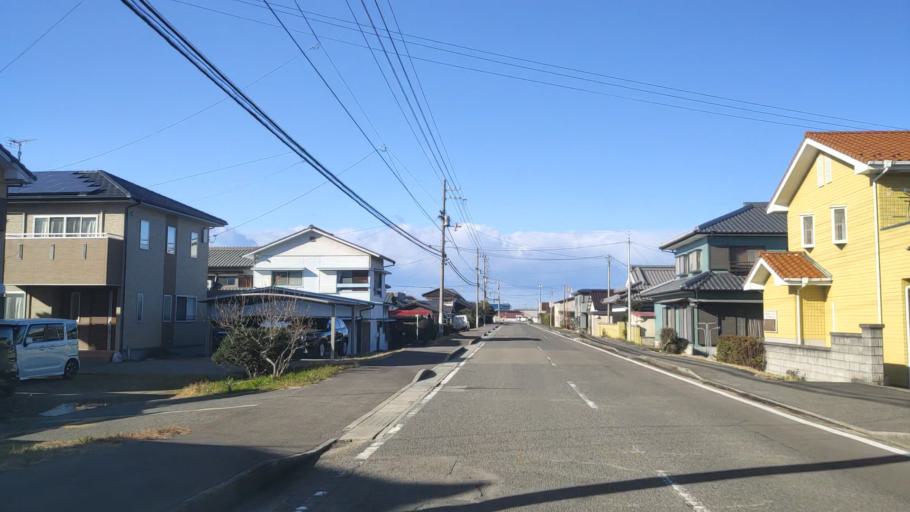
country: JP
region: Ehime
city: Saijo
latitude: 33.9291
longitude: 133.1652
